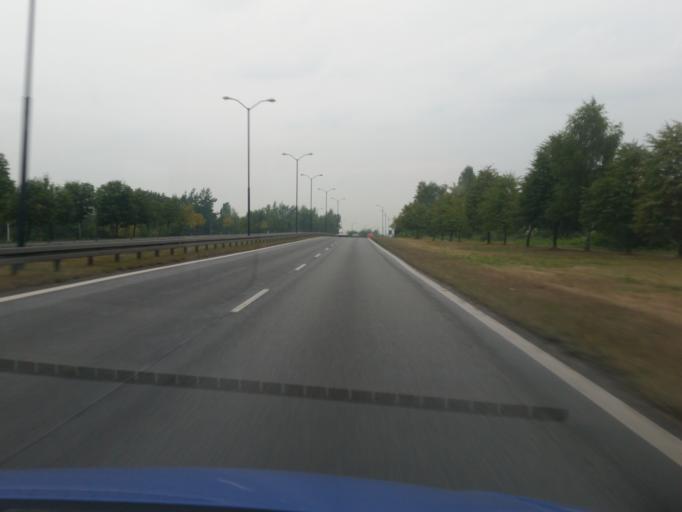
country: PL
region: Silesian Voivodeship
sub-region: Sosnowiec
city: Sosnowiec
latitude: 50.2553
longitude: 19.0851
